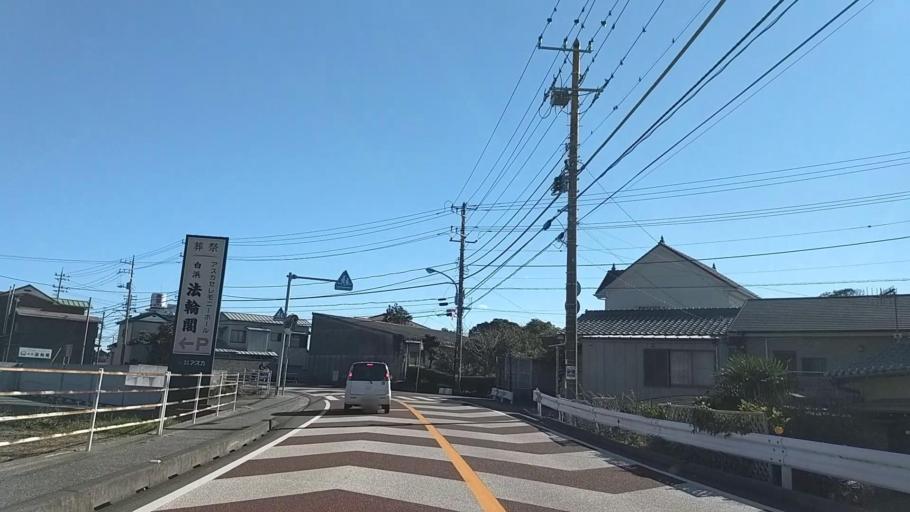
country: JP
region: Chiba
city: Tateyama
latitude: 34.9075
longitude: 139.8911
